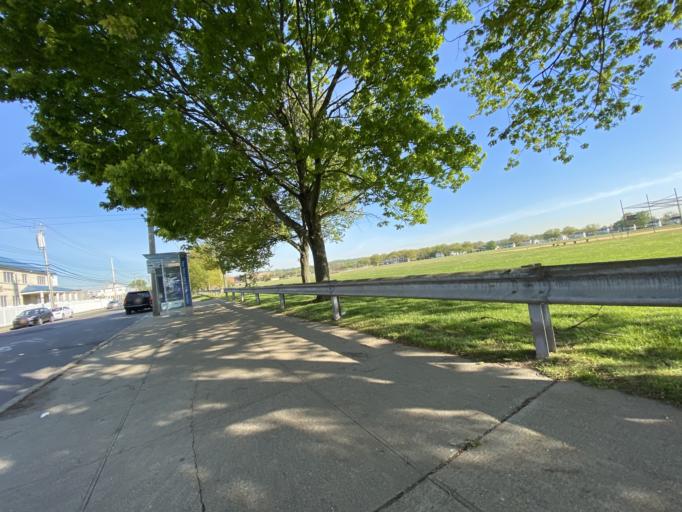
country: US
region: New York
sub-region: Richmond County
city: Staten Island
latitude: 40.5666
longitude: -74.1018
